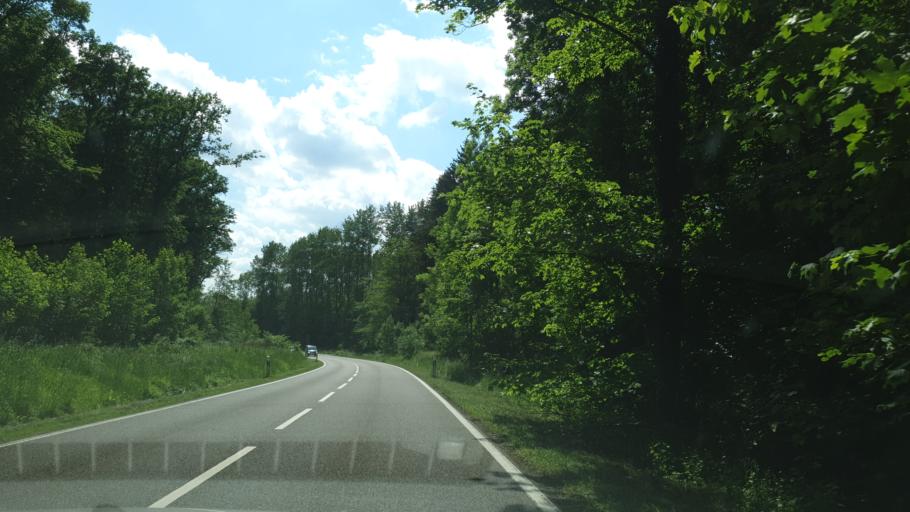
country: DE
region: Rheinland-Pfalz
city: Siershahn
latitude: 50.4917
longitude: 7.7846
